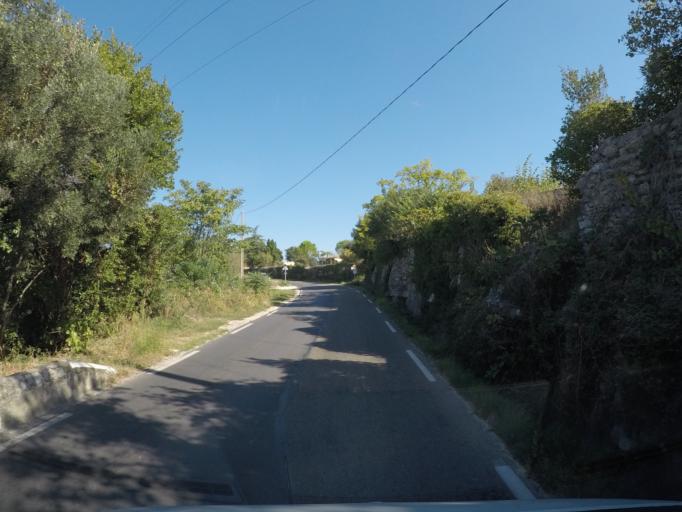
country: FR
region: Languedoc-Roussillon
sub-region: Departement du Gard
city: Uzes
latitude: 44.0082
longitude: 4.4049
